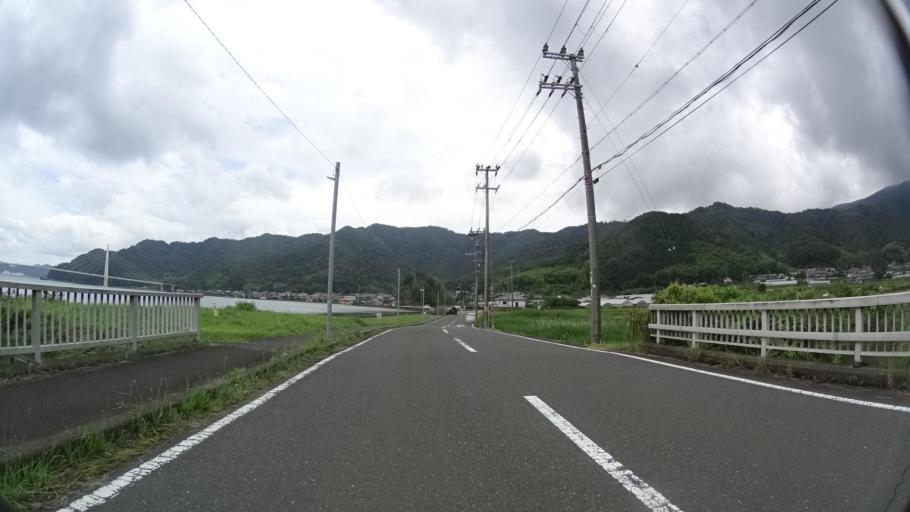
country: JP
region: Kyoto
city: Maizuru
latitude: 35.5068
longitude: 135.3782
